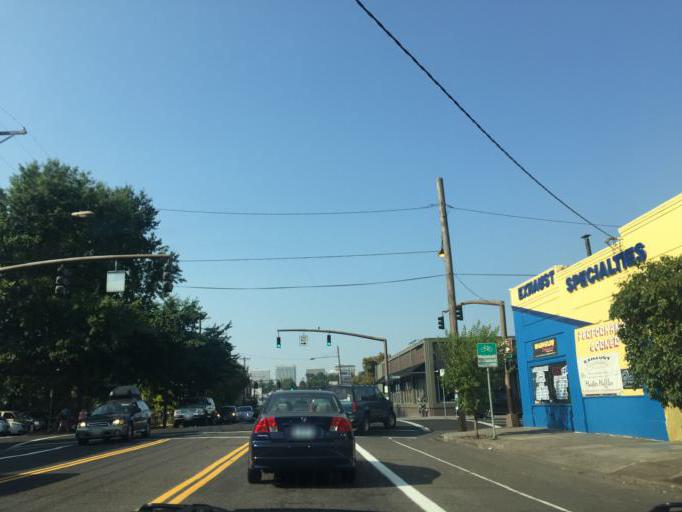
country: US
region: Oregon
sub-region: Multnomah County
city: Portland
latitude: 45.5162
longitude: -122.6587
